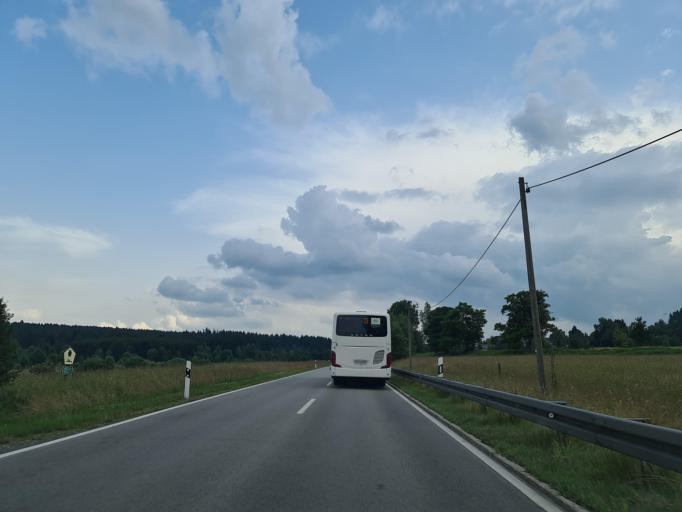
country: DE
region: Saxony
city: Hammerbrucke
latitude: 50.4206
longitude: 12.3991
